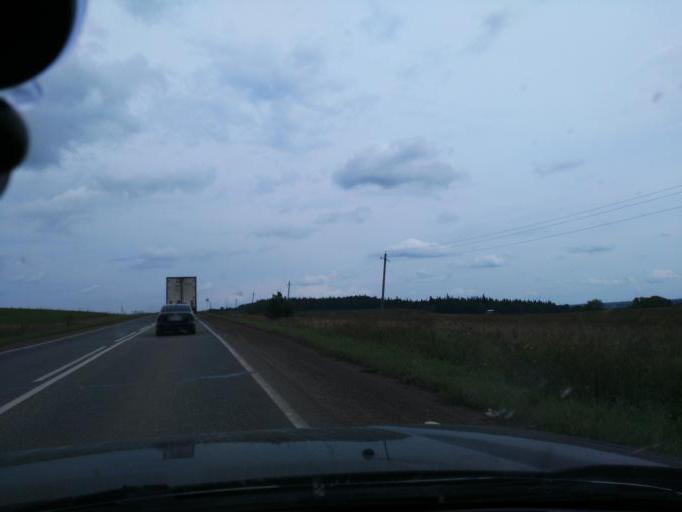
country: RU
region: Perm
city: Kuyeda
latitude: 56.4628
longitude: 55.6596
